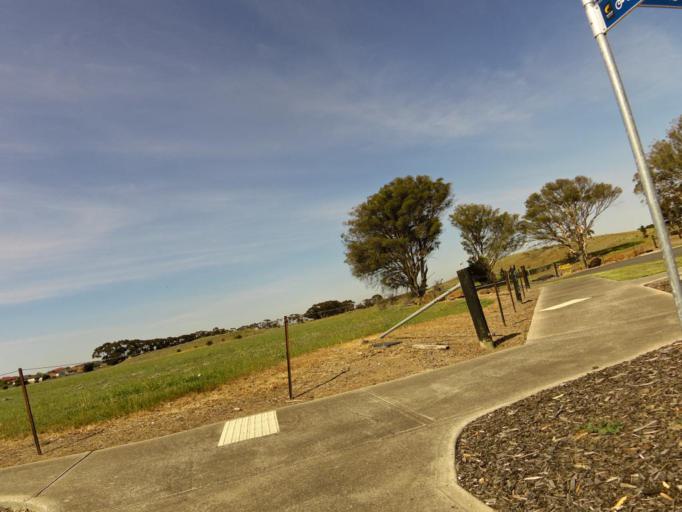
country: AU
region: Victoria
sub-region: Brimbank
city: Deer Park
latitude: -37.7676
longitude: 144.7904
